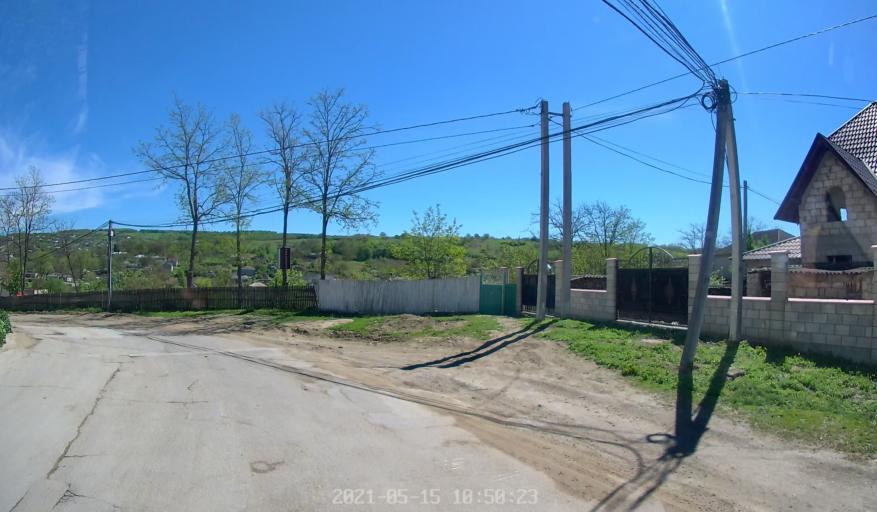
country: MD
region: Hincesti
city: Hincesti
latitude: 46.8241
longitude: 28.6742
